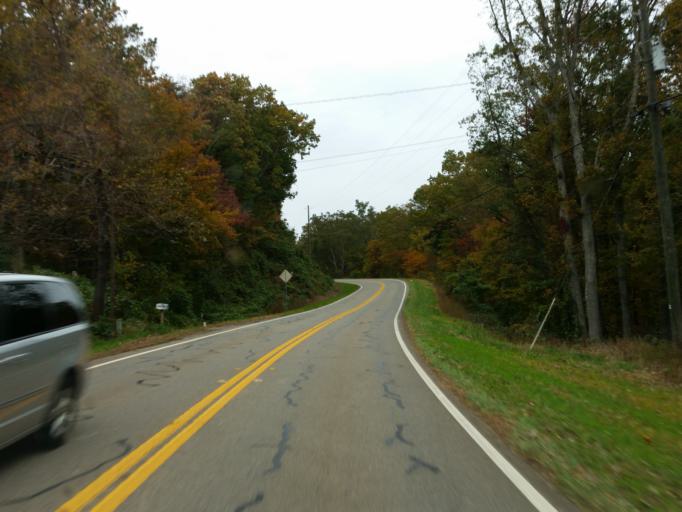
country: US
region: Georgia
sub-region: Pickens County
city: Jasper
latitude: 34.5265
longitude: -84.4166
